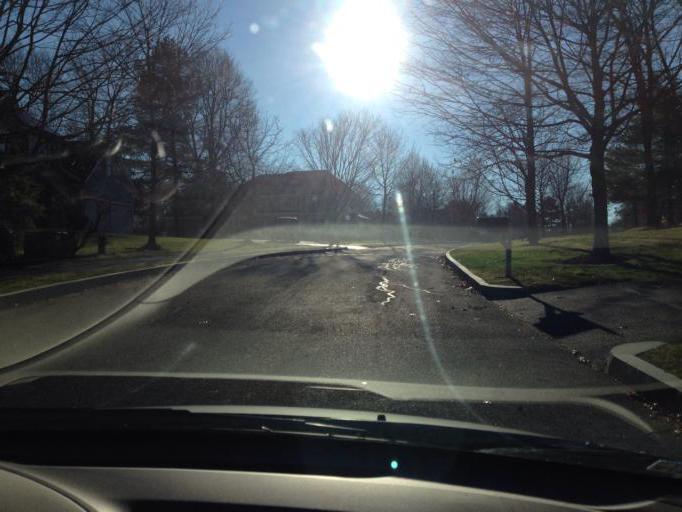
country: US
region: Massachusetts
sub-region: Middlesex County
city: Bedford
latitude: 42.5211
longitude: -71.2813
